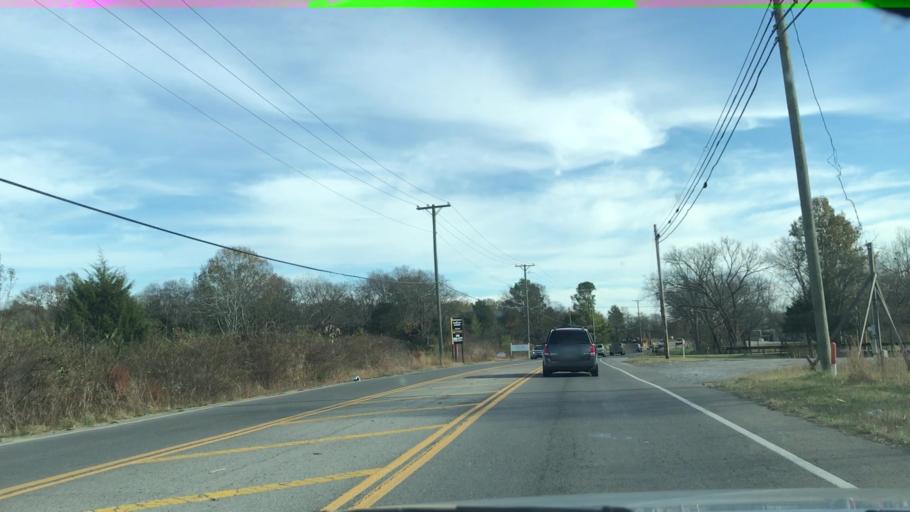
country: US
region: Tennessee
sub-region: Williamson County
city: Nolensville
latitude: 35.9952
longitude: -86.6875
